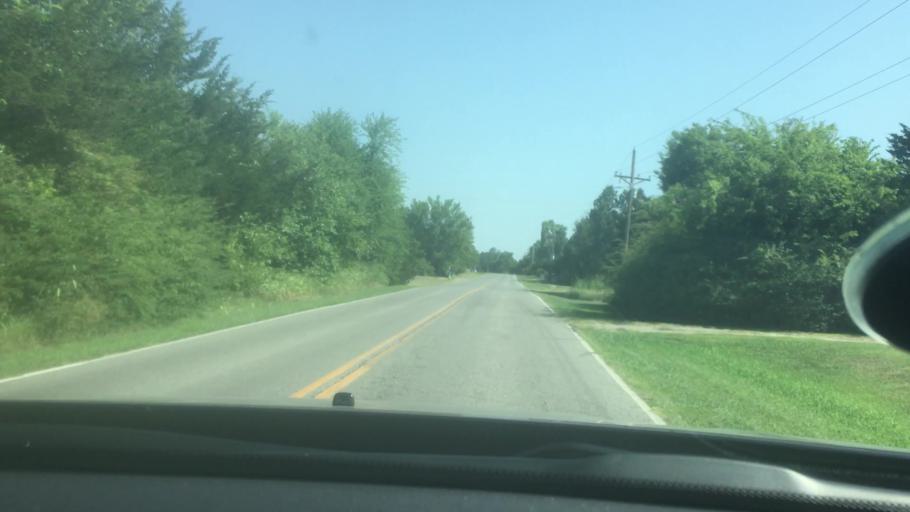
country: US
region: Oklahoma
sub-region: Bryan County
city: Calera
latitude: 34.0229
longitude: -96.4742
